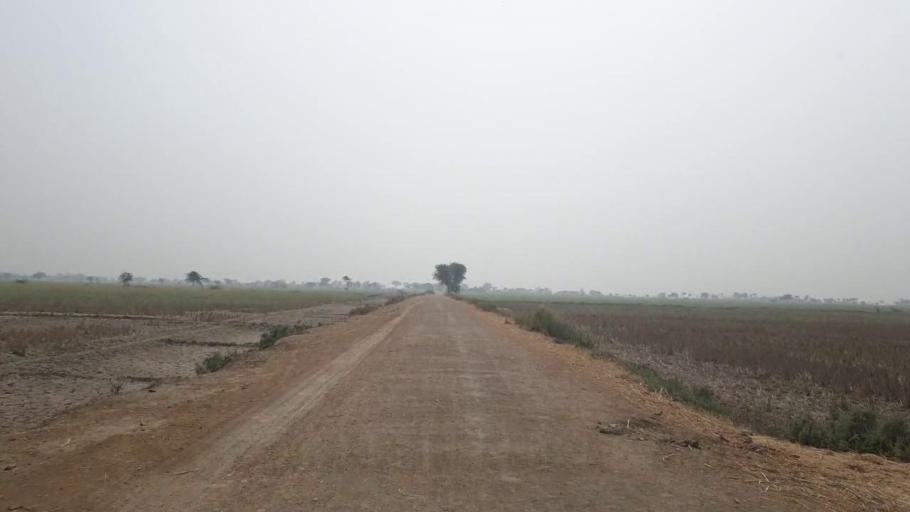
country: PK
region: Sindh
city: Kario
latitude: 24.6517
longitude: 68.6217
